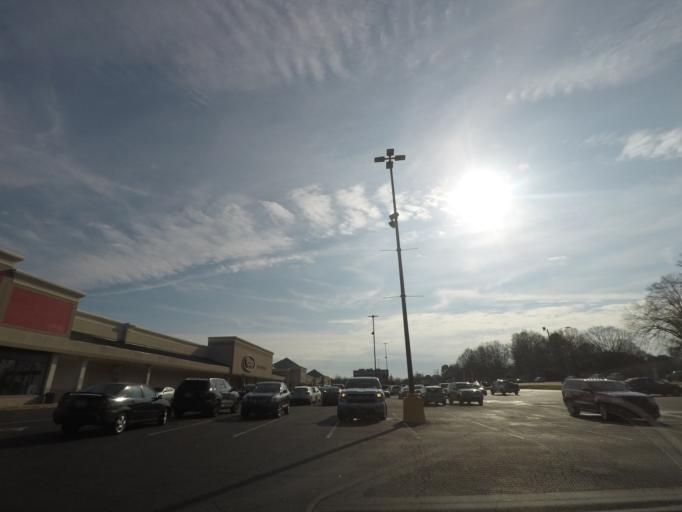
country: US
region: North Carolina
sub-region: Durham County
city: Durham
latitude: 36.0502
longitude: -78.9053
